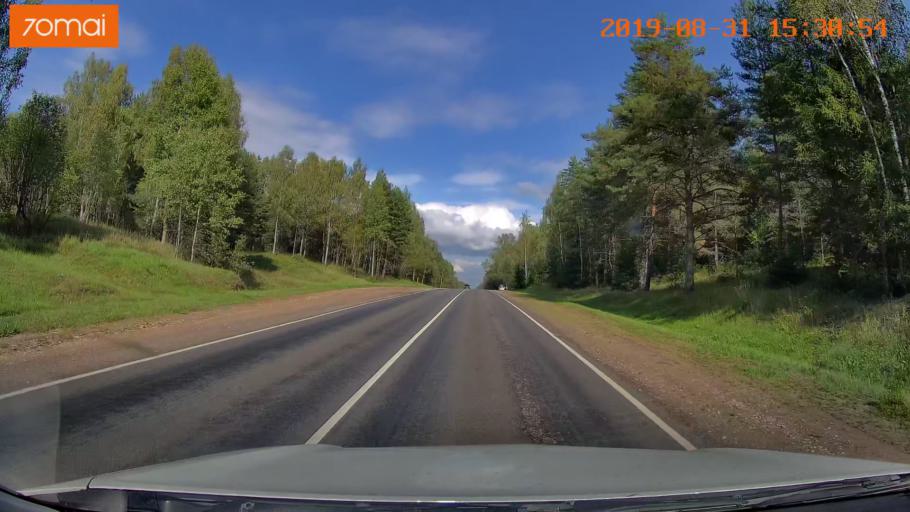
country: RU
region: Kaluga
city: Baryatino
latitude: 54.5788
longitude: 34.6414
